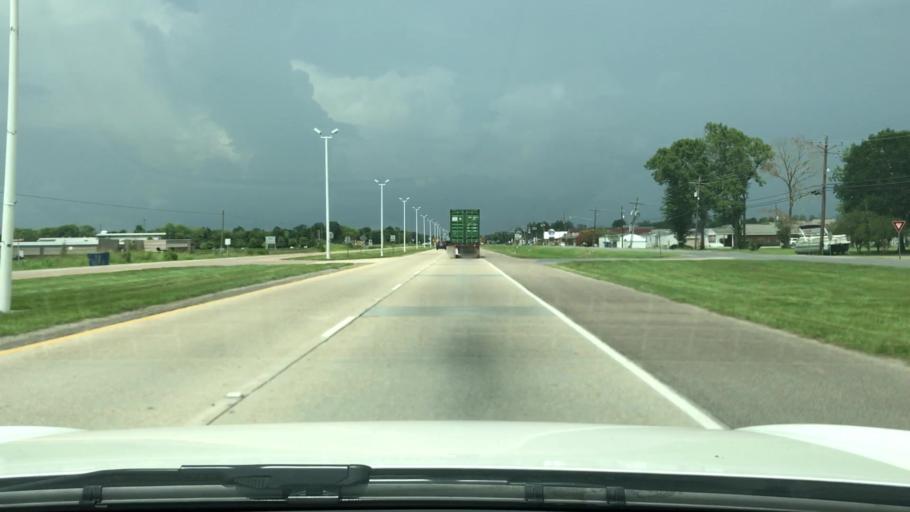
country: US
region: Louisiana
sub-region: West Baton Rouge Parish
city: Addis
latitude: 30.3702
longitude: -91.2569
